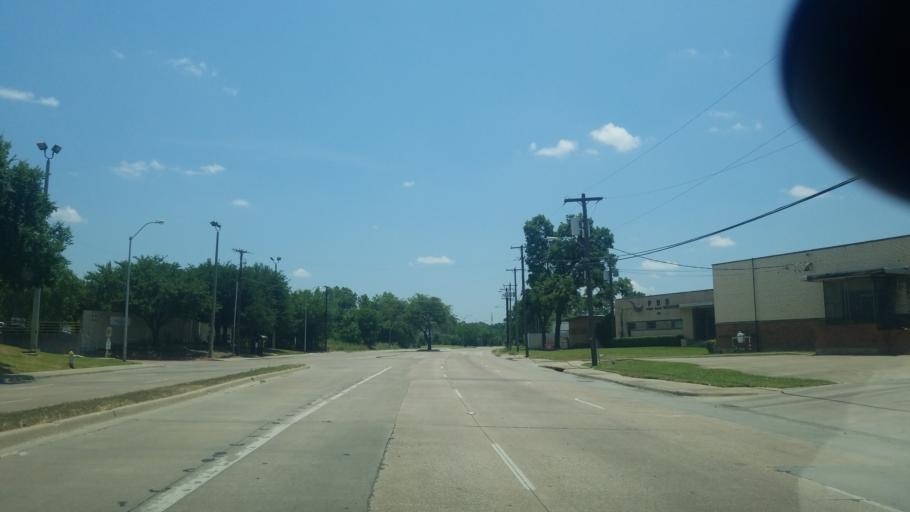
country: US
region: Texas
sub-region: Dallas County
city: Dallas
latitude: 32.7333
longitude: -96.7853
